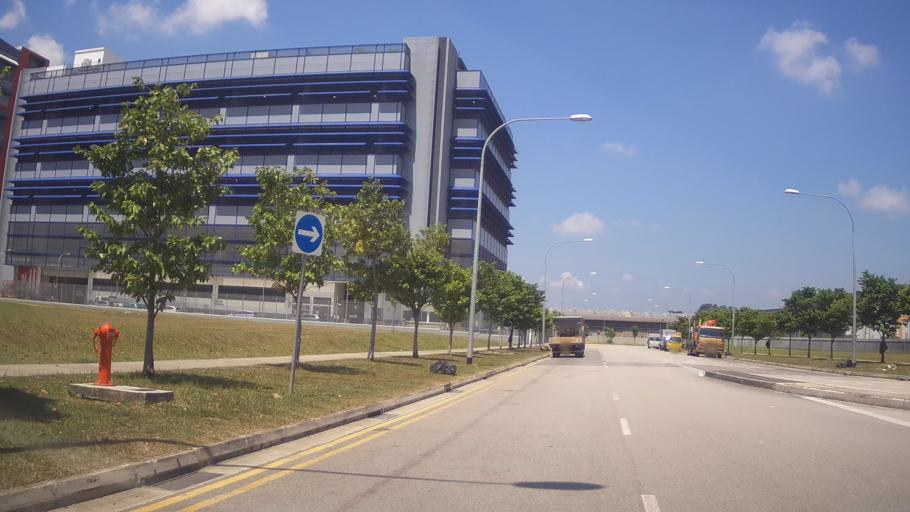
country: SG
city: Singapore
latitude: 1.3176
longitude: 103.7242
